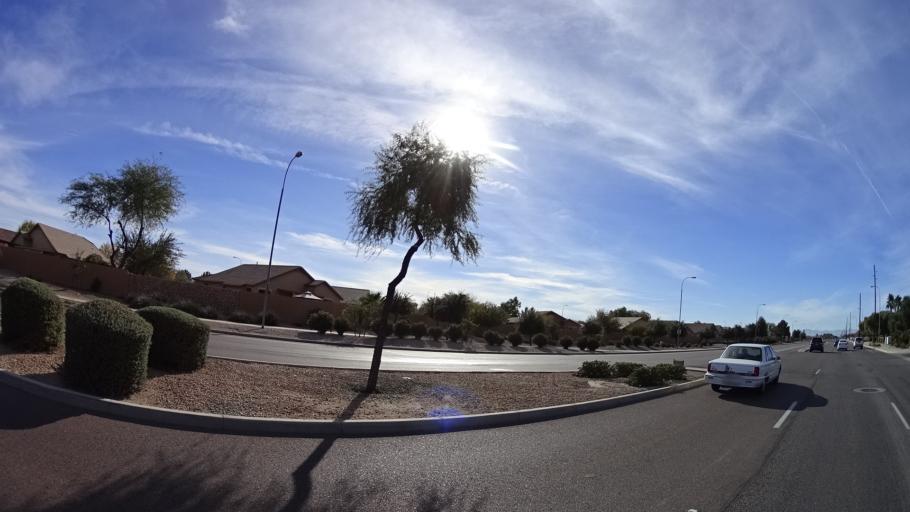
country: US
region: Arizona
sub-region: Maricopa County
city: Sun Lakes
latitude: 33.2192
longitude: -111.7660
